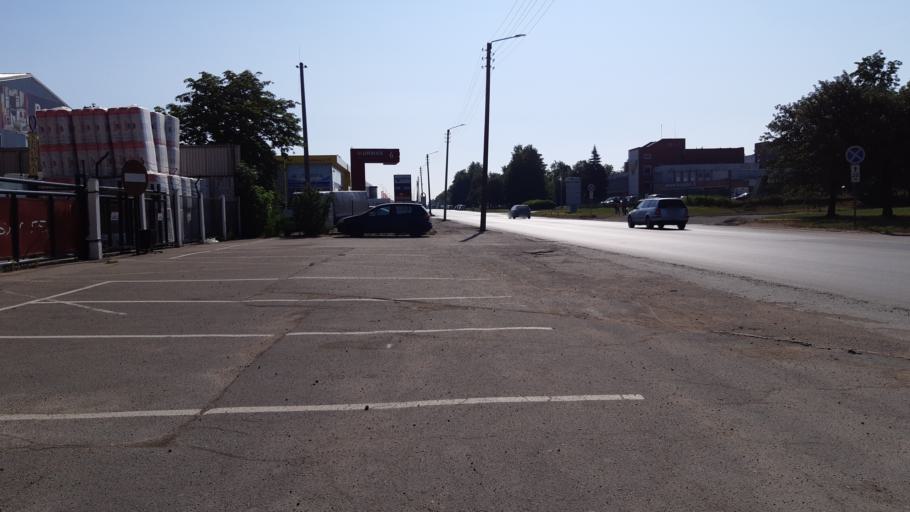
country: LT
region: Kauno apskritis
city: Dainava (Kaunas)
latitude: 54.9136
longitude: 23.9907
